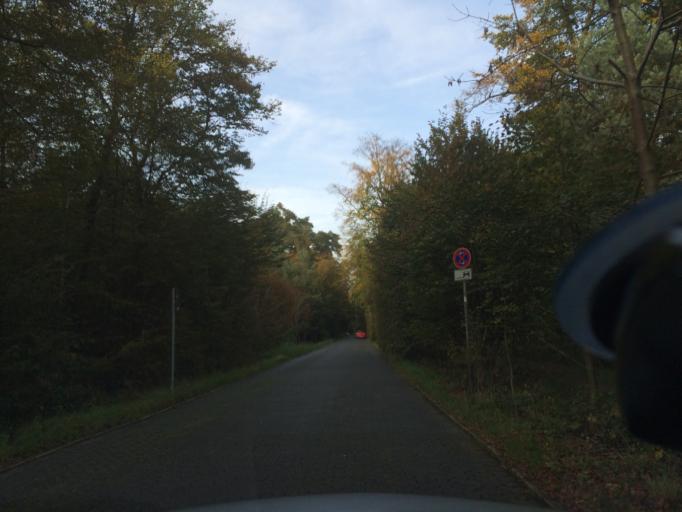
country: DE
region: Hesse
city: Morfelden-Walldorf
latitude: 49.9665
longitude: 8.5504
